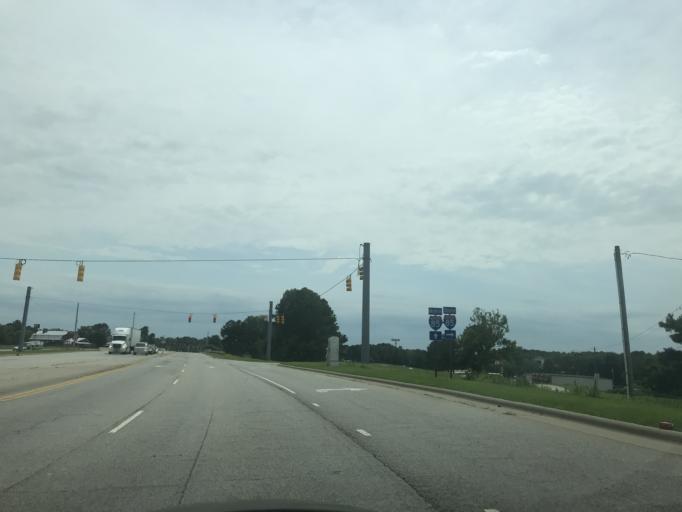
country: US
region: North Carolina
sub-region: Vance County
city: South Henderson
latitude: 36.3289
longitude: -78.4487
